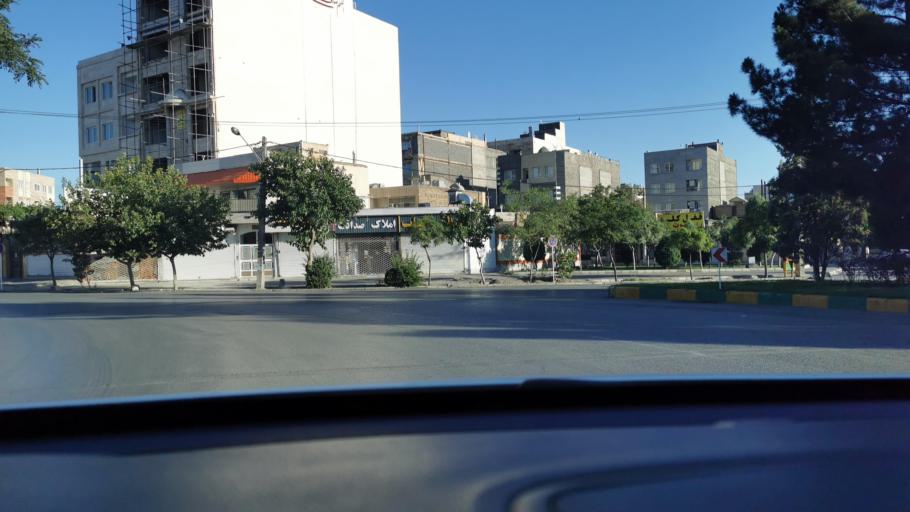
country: IR
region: Razavi Khorasan
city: Mashhad
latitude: 36.3565
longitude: 59.4881
